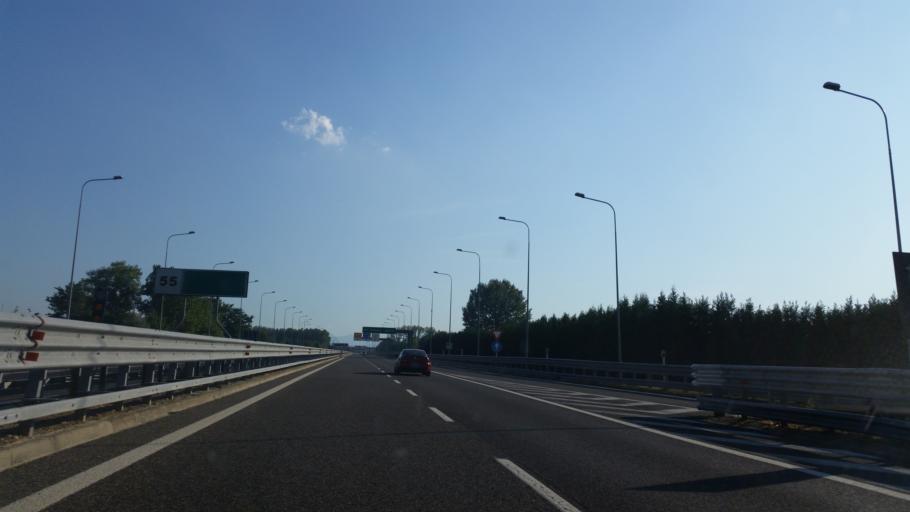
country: IT
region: Piedmont
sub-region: Provincia di Cuneo
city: Govone
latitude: 44.7763
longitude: 8.1089
